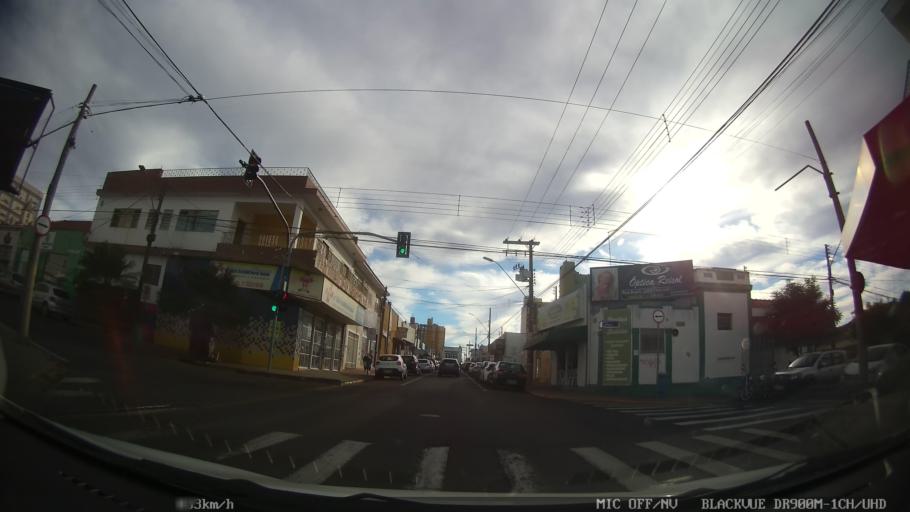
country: BR
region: Sao Paulo
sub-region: Catanduva
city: Catanduva
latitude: -21.1420
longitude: -48.9747
